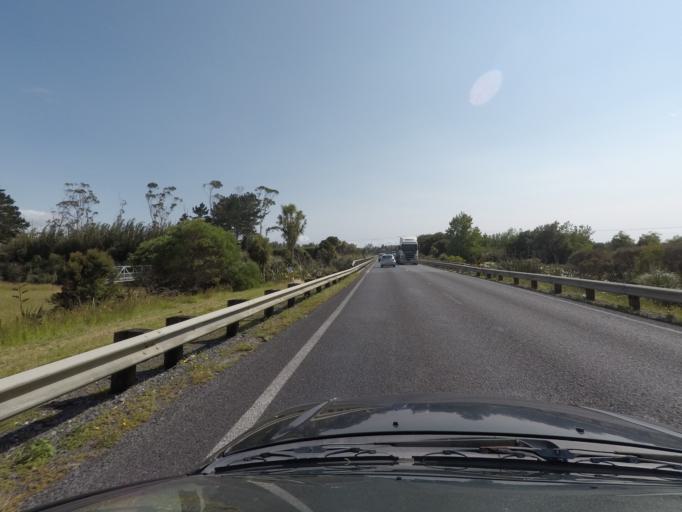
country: NZ
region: Northland
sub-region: Whangarei
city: Ruakaka
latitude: -35.9656
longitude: 174.4449
